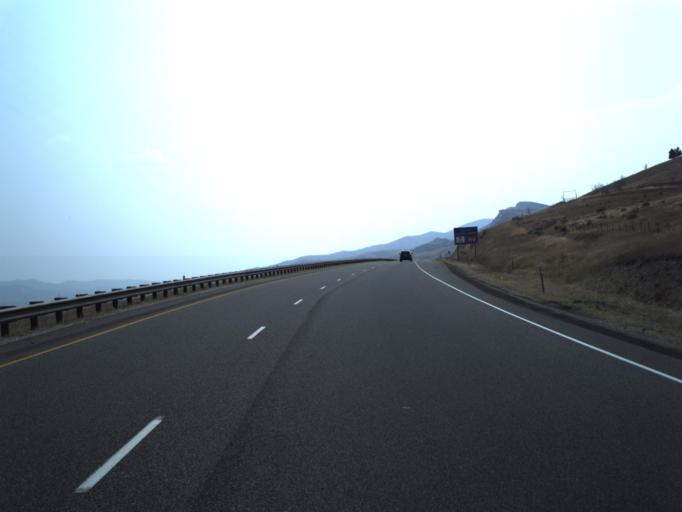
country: US
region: Utah
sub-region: Summit County
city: Coalville
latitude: 40.9354
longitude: -111.4096
